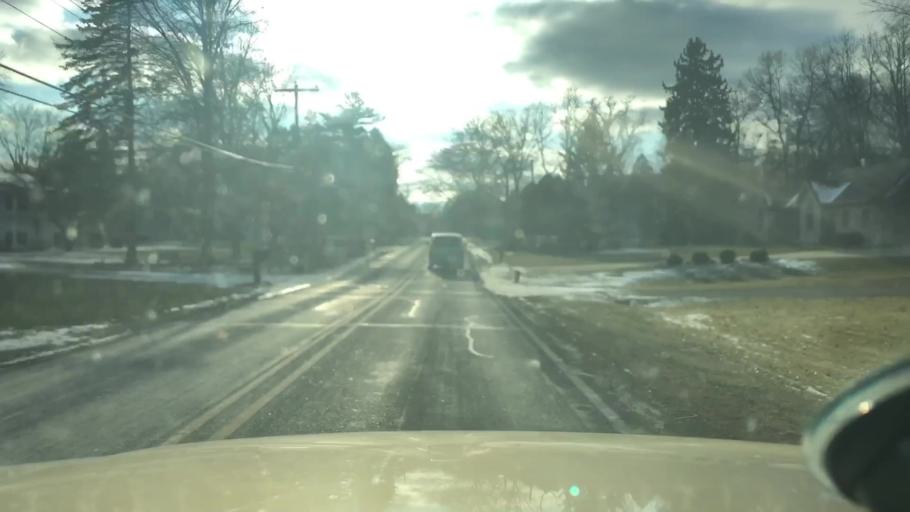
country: US
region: Michigan
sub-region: Jackson County
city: Vandercook Lake
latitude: 42.1961
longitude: -84.4461
